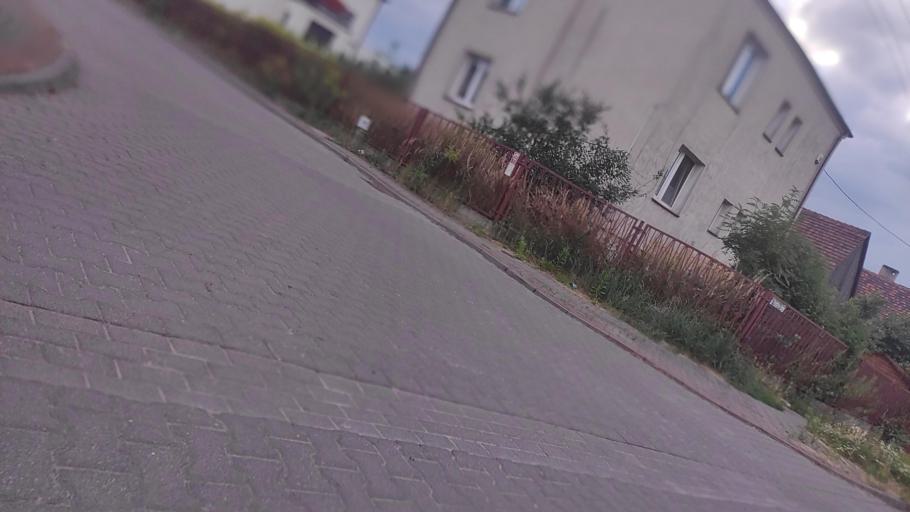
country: PL
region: Greater Poland Voivodeship
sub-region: Powiat poznanski
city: Swarzedz
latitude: 52.4041
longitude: 17.0798
